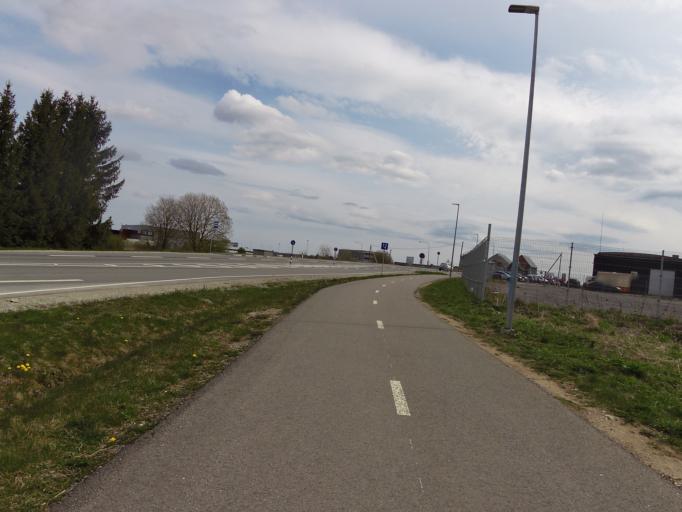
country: EE
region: Harju
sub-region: Rae vald
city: Jueri
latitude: 59.3820
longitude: 24.8292
